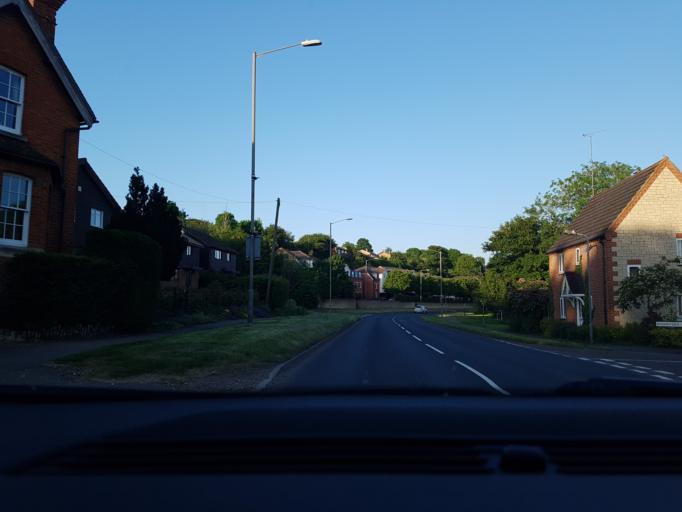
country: GB
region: England
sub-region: Buckinghamshire
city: Buckingham
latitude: 52.0029
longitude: -0.9816
